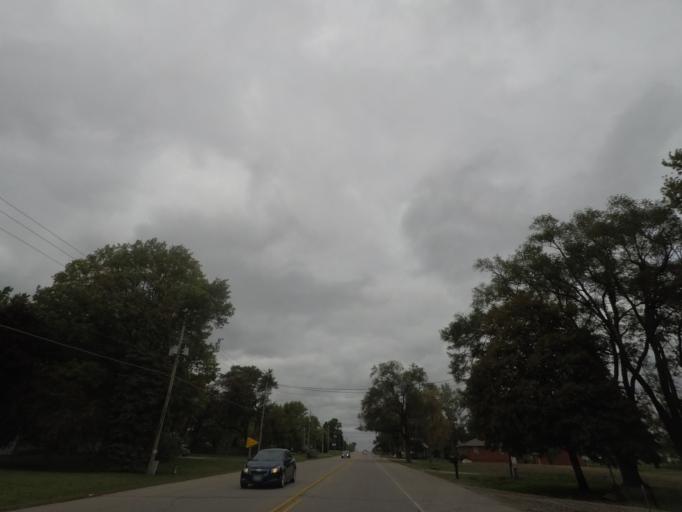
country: US
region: Iowa
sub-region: Polk County
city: Saylorville
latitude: 41.6907
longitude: -93.6006
